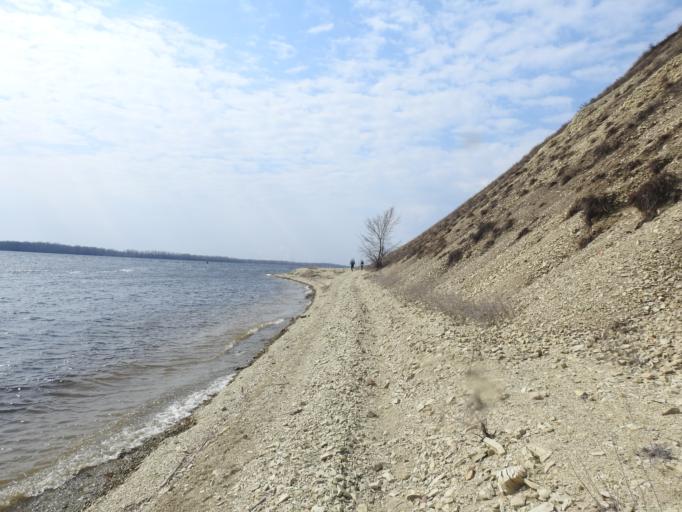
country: RU
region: Saratov
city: Voskresenskoye
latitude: 51.8025
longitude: 46.9066
